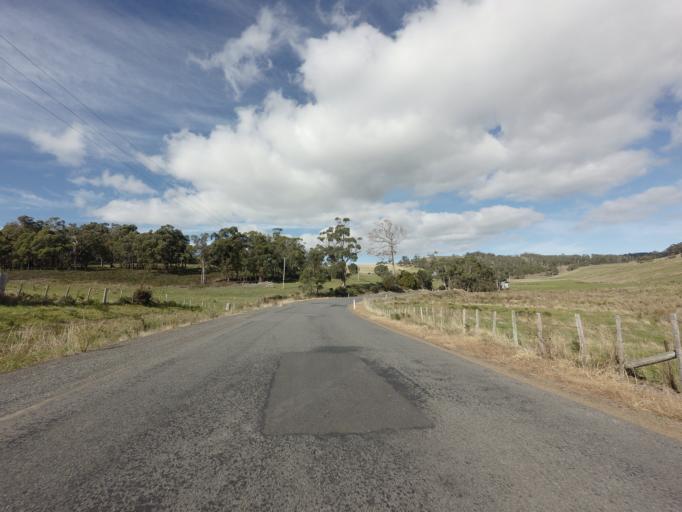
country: AU
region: Tasmania
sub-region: Clarence
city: Sandford
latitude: -43.0338
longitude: 147.7315
